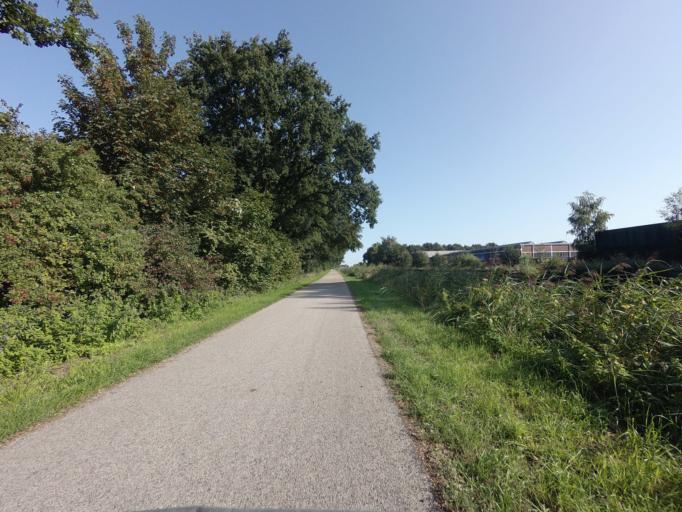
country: NL
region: Overijssel
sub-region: Gemeente Raalte
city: Raalte
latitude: 52.3745
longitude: 6.2778
